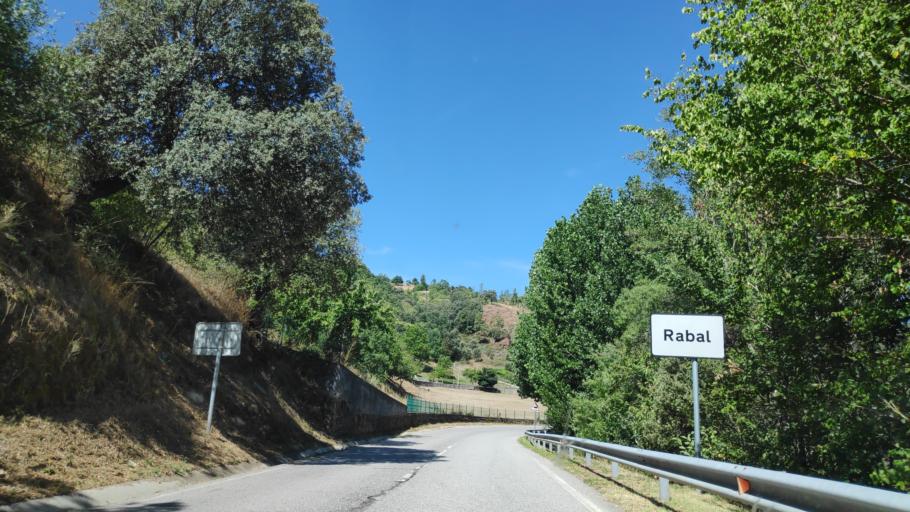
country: PT
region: Braganca
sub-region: Braganca Municipality
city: Braganca
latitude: 41.8626
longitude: -6.7463
